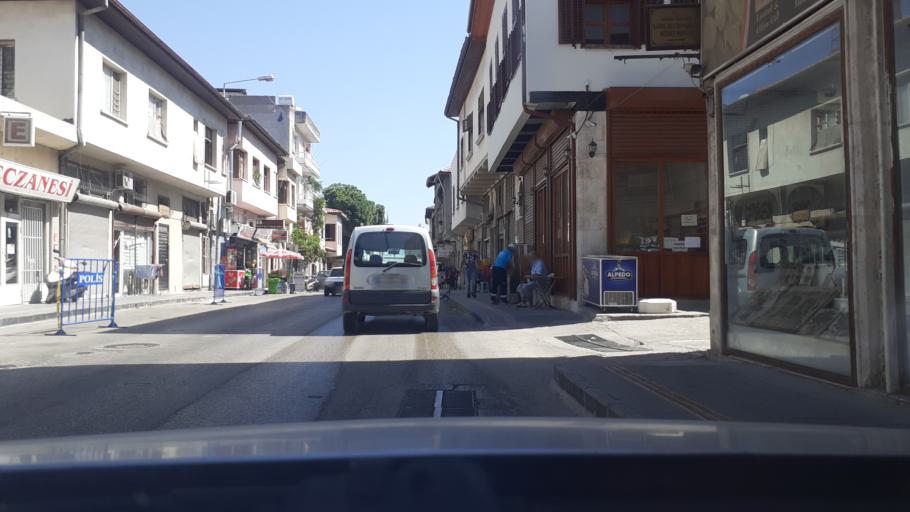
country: TR
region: Hatay
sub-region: Antakya Ilcesi
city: Antakya
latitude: 36.1999
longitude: 36.1640
